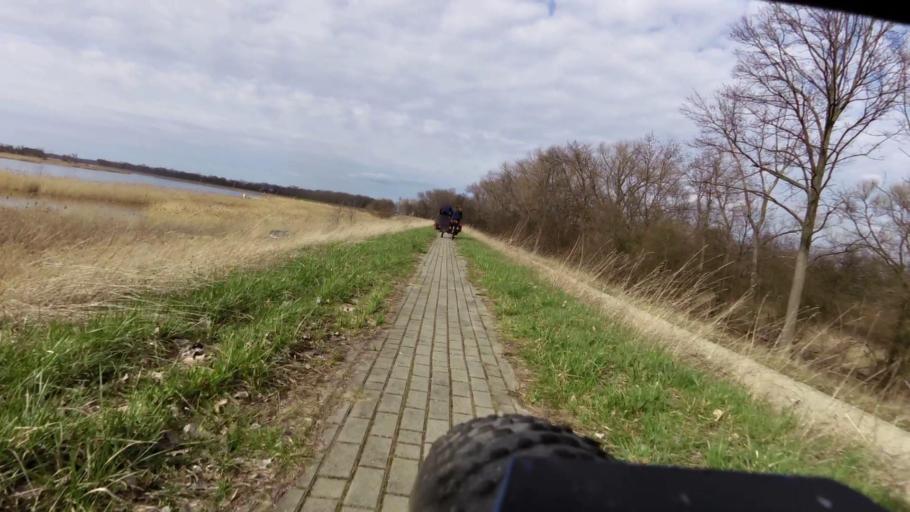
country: PL
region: Lubusz
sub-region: Powiat slubicki
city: Gorzyca
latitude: 52.4964
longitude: 14.6382
